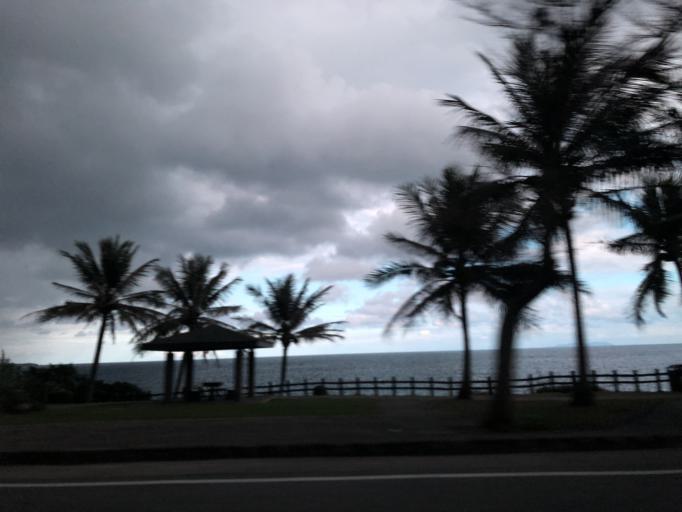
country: TW
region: Taiwan
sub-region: Taitung
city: Taitung
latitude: 22.8575
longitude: 121.1985
